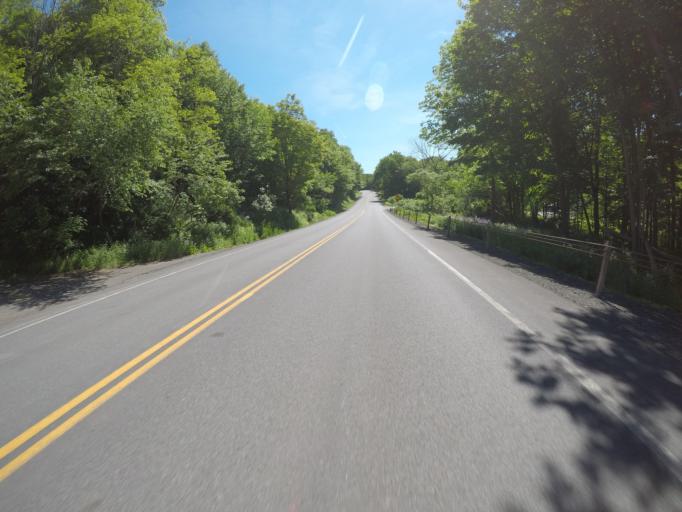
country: US
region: New York
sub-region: Delaware County
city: Delhi
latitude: 42.2567
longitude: -74.9423
